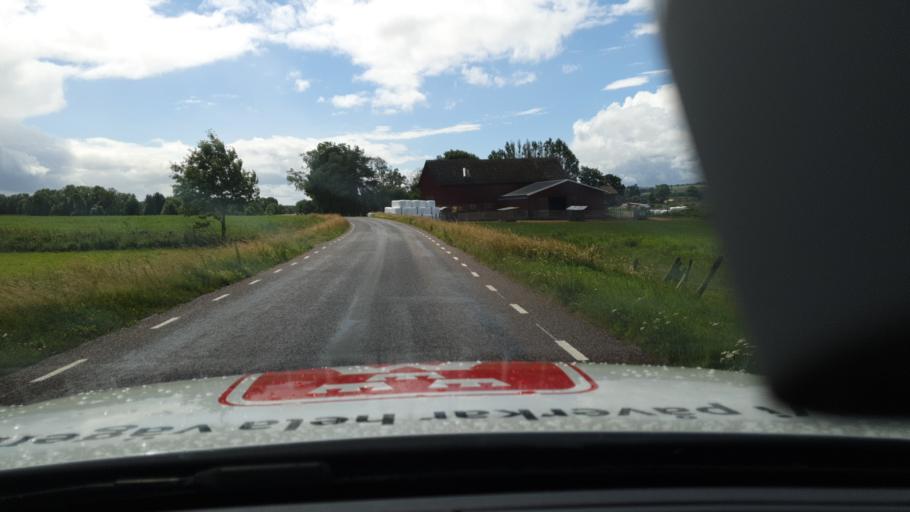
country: SE
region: Vaestra Goetaland
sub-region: Falkopings Kommun
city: Akarp
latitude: 58.1832
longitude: 13.6974
